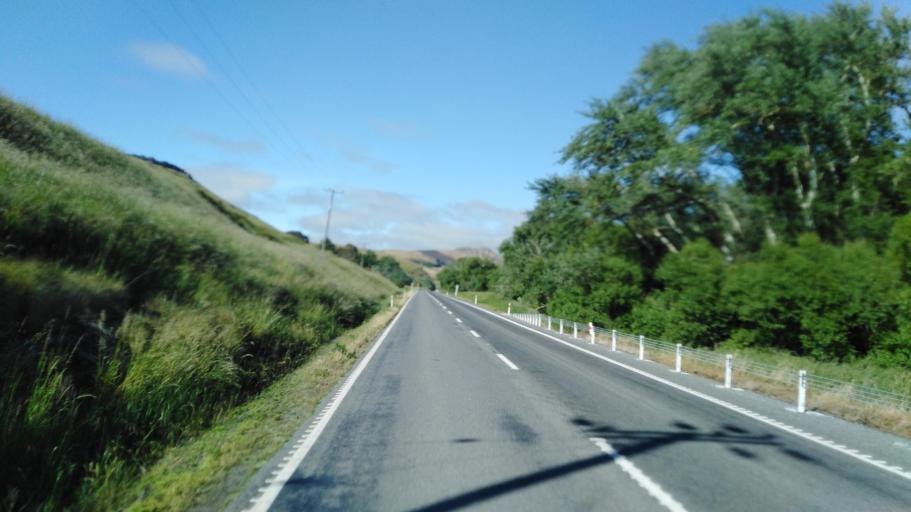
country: NZ
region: Canterbury
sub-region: Hurunui District
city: Amberley
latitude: -43.0015
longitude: 172.7120
